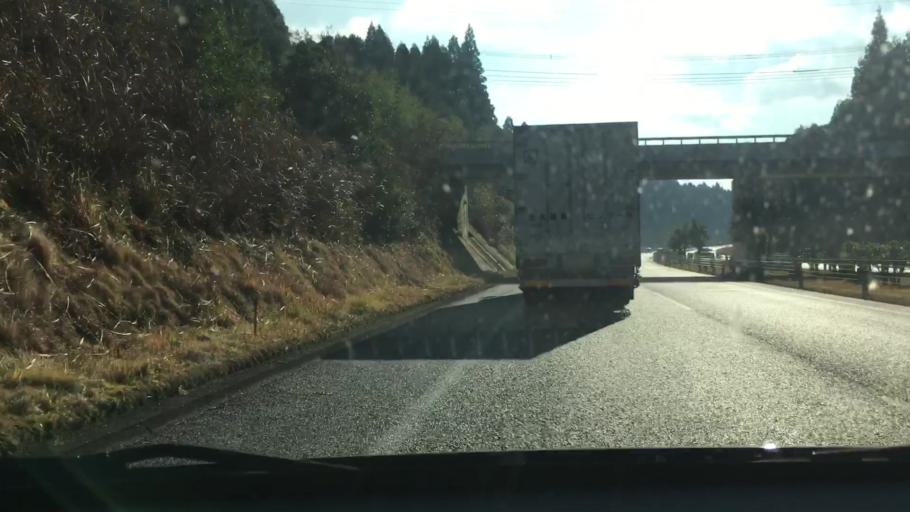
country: JP
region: Kagoshima
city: Okuchi-shinohara
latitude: 31.9624
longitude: 130.7449
